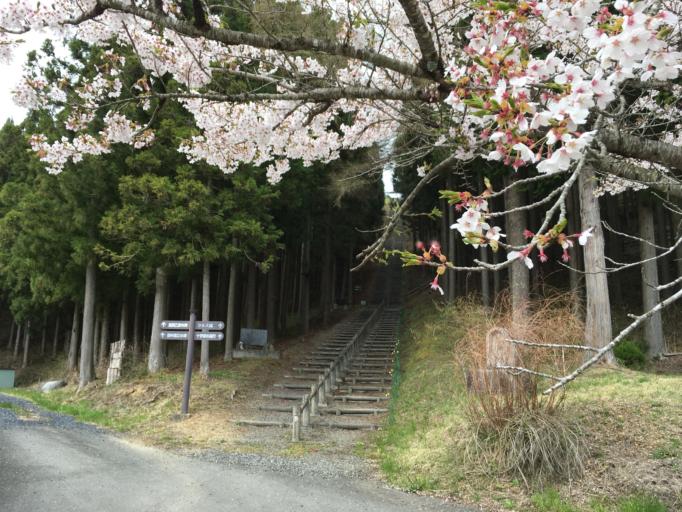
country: JP
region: Iwate
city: Ichinoseki
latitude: 38.7936
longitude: 141.4049
